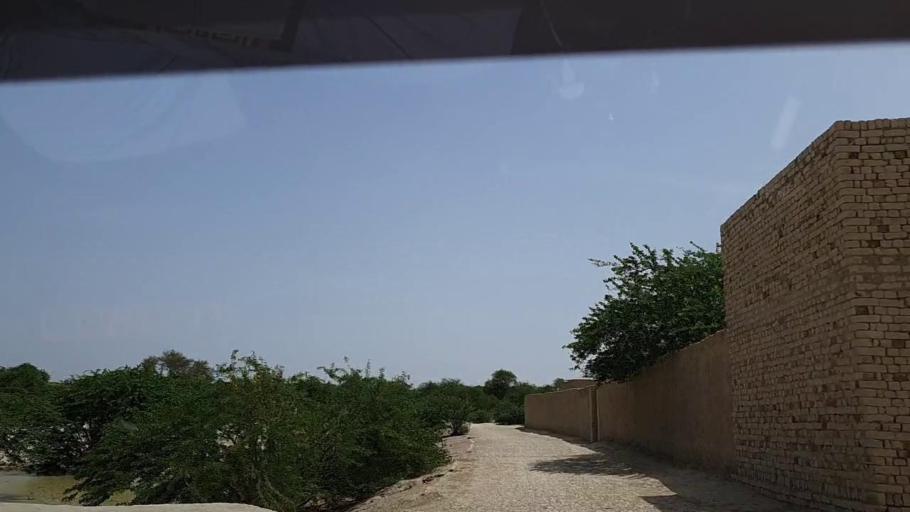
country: PK
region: Sindh
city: Johi
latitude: 26.7147
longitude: 67.6516
